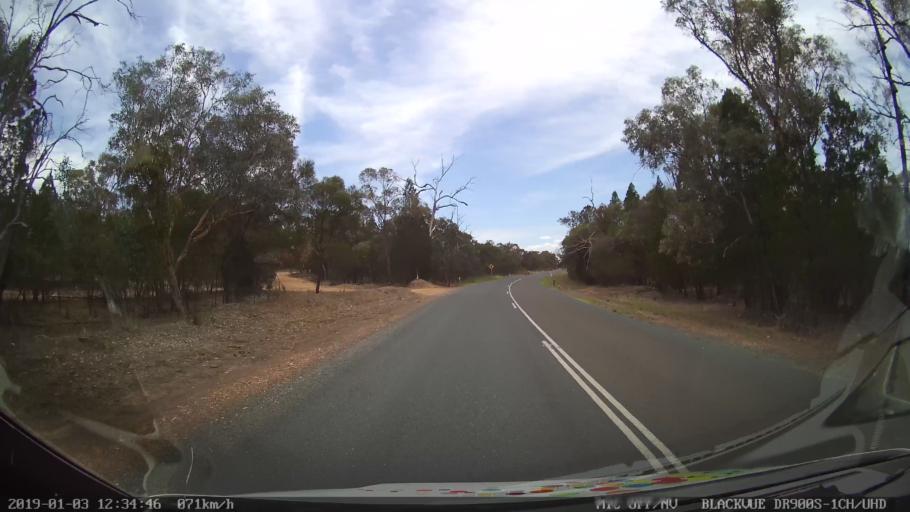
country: AU
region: New South Wales
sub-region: Weddin
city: Grenfell
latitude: -33.8730
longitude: 148.1663
